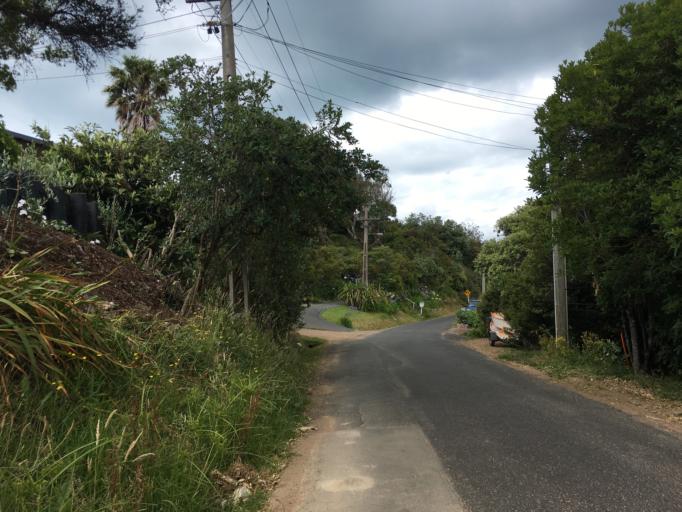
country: NZ
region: Auckland
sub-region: Auckland
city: Pakuranga
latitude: -36.7913
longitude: 175.0196
